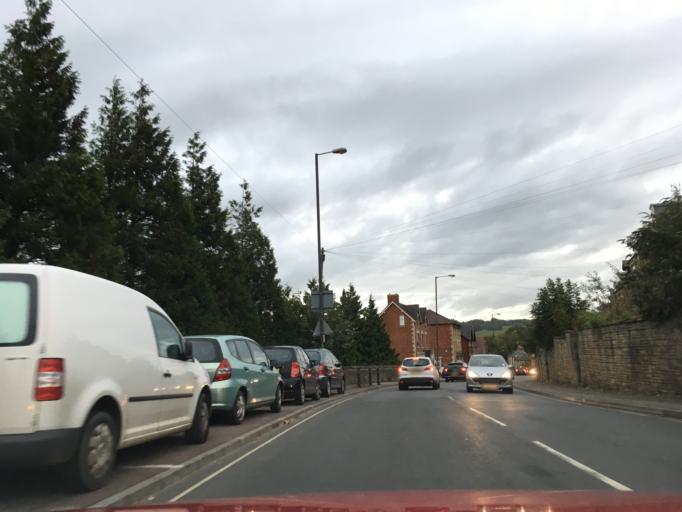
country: GB
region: England
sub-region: Gloucestershire
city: Stroud
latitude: 51.7393
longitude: -2.2311
